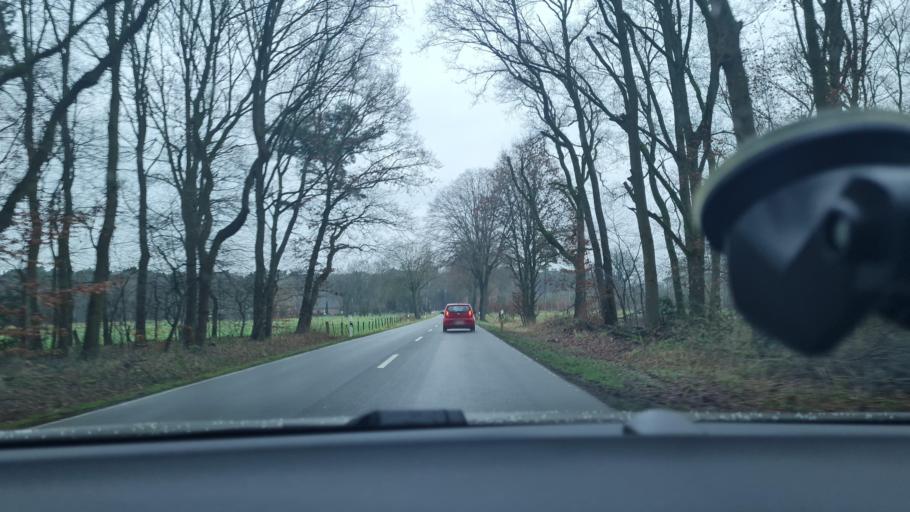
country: DE
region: North Rhine-Westphalia
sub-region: Regierungsbezirk Dusseldorf
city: Hunxe
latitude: 51.6790
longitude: 6.7409
